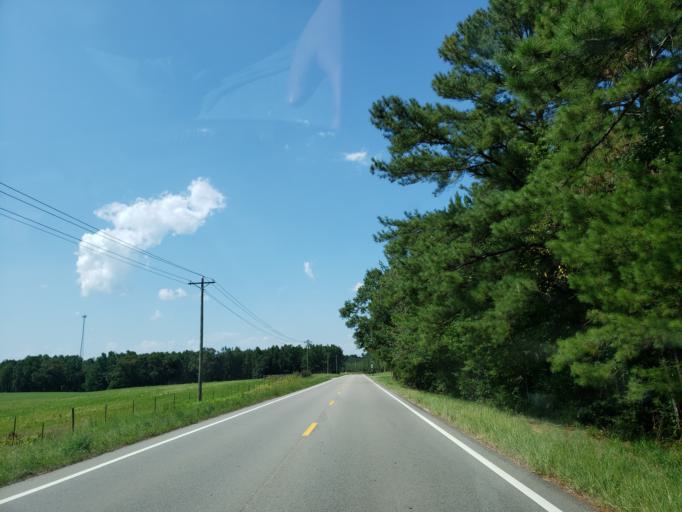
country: US
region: Mississippi
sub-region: Lamar County
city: Sumrall
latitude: 31.3579
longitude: -89.4982
